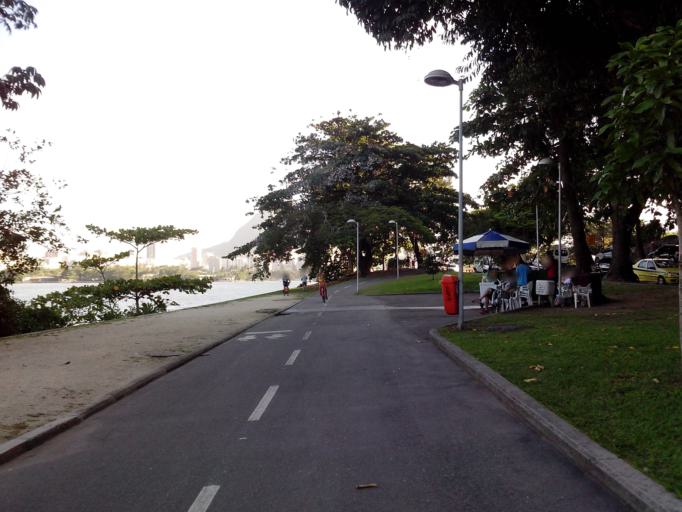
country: BR
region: Rio de Janeiro
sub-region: Rio De Janeiro
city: Rio de Janeiro
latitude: -22.9744
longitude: -43.2062
